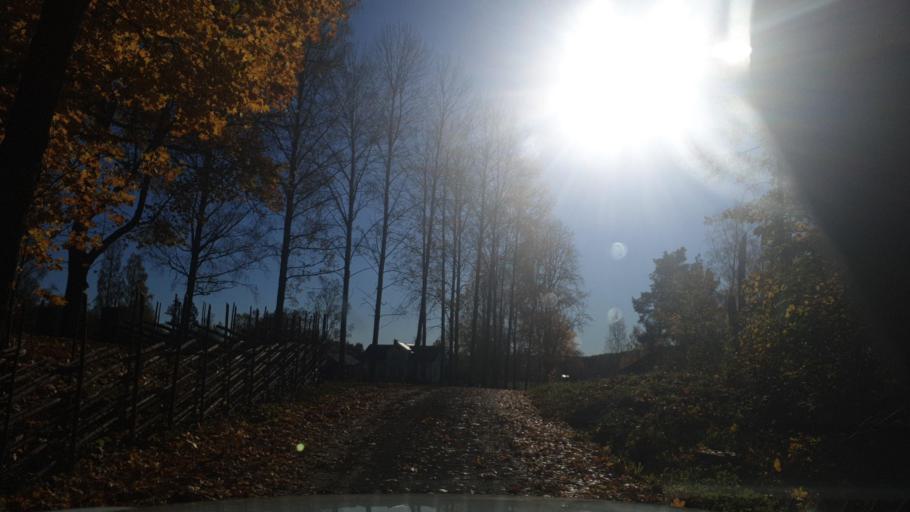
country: SE
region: Vaermland
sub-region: Grums Kommun
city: Grums
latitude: 59.4899
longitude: 12.9291
